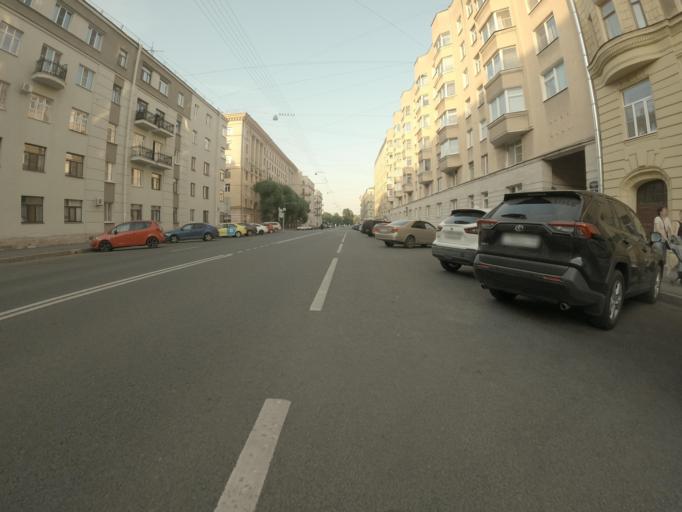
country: RU
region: St.-Petersburg
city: Centralniy
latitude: 59.9468
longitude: 30.3850
